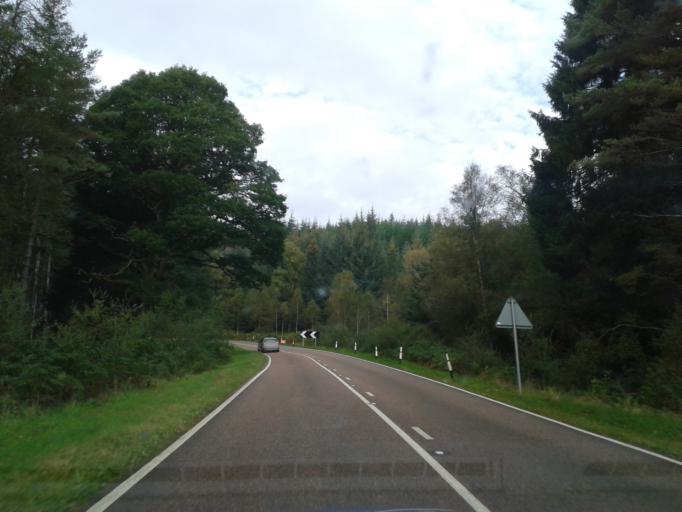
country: GB
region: Scotland
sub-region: Highland
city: Spean Bridge
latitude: 57.0740
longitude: -4.8343
